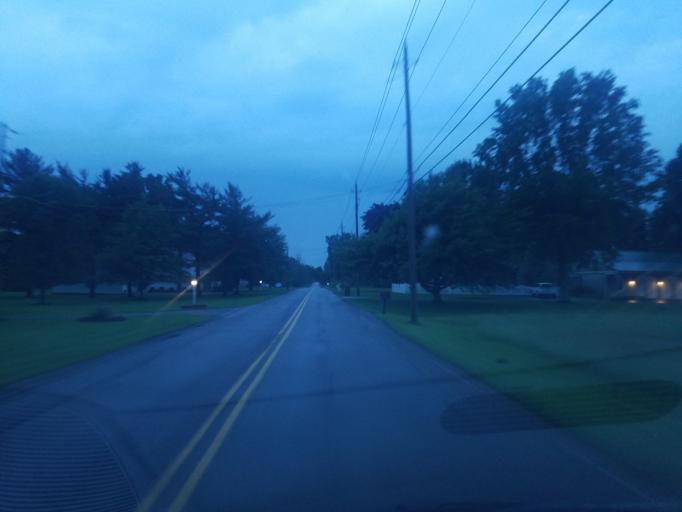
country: US
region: Ohio
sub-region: Mahoning County
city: Boardman
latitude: 40.9974
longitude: -80.7114
